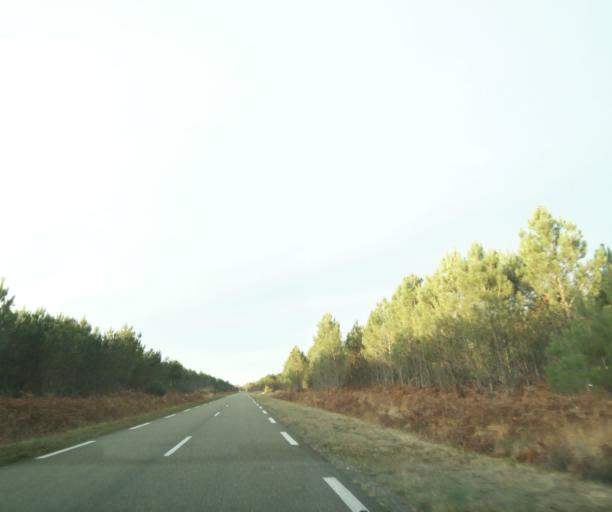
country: FR
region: Aquitaine
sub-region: Departement des Landes
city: Roquefort
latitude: 44.1827
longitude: -0.1476
